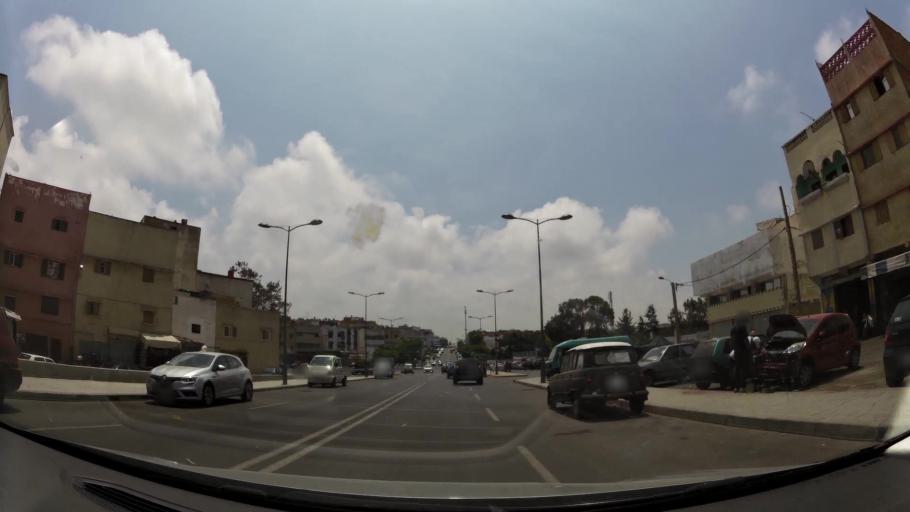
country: MA
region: Rabat-Sale-Zemmour-Zaer
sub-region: Rabat
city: Rabat
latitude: 33.9867
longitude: -6.8774
